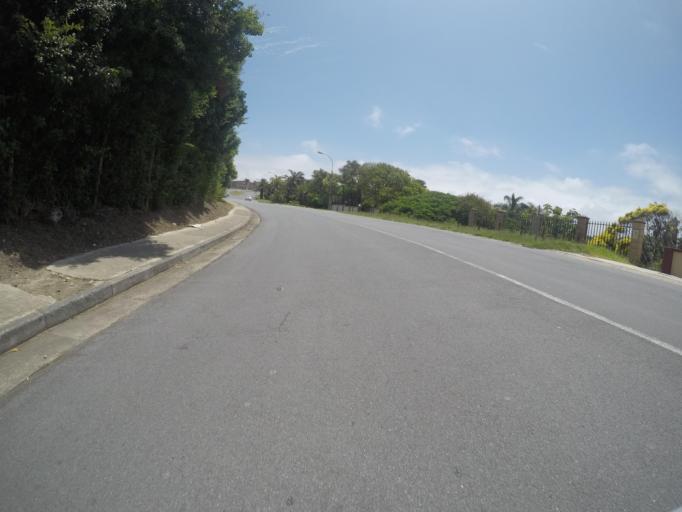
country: ZA
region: Eastern Cape
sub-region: Buffalo City Metropolitan Municipality
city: East London
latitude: -33.0027
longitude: 27.9237
